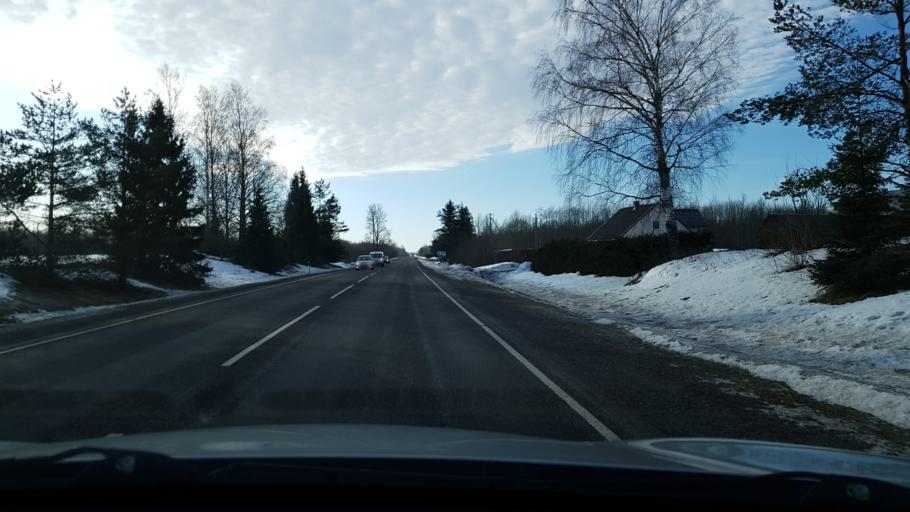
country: EE
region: Viljandimaa
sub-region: Viljandi linn
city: Viljandi
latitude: 58.4214
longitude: 25.5980
